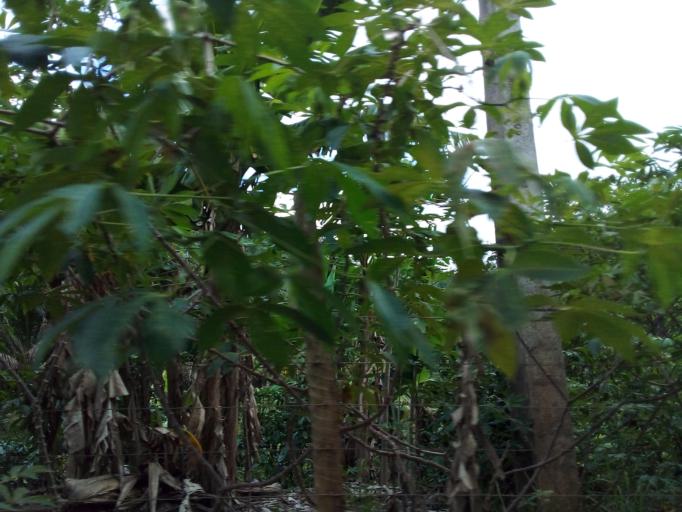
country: BR
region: Espirito Santo
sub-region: Joao Neiva
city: Joao Neiva
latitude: -19.7509
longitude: -40.3665
